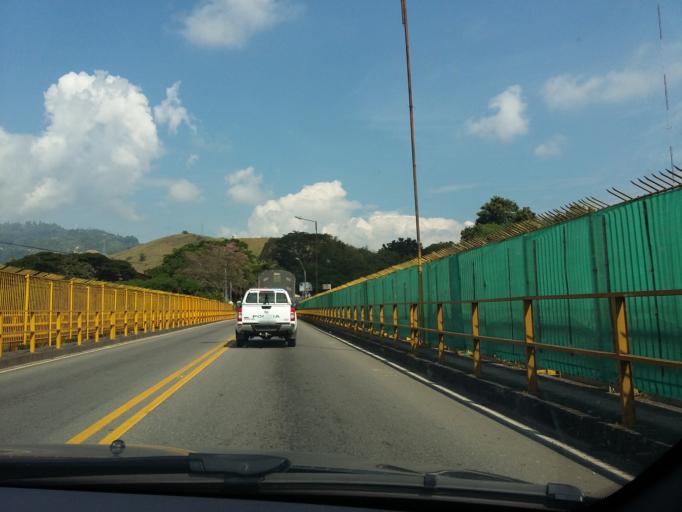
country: CO
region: Tolima
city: Ibague
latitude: 4.4055
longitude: -75.1820
